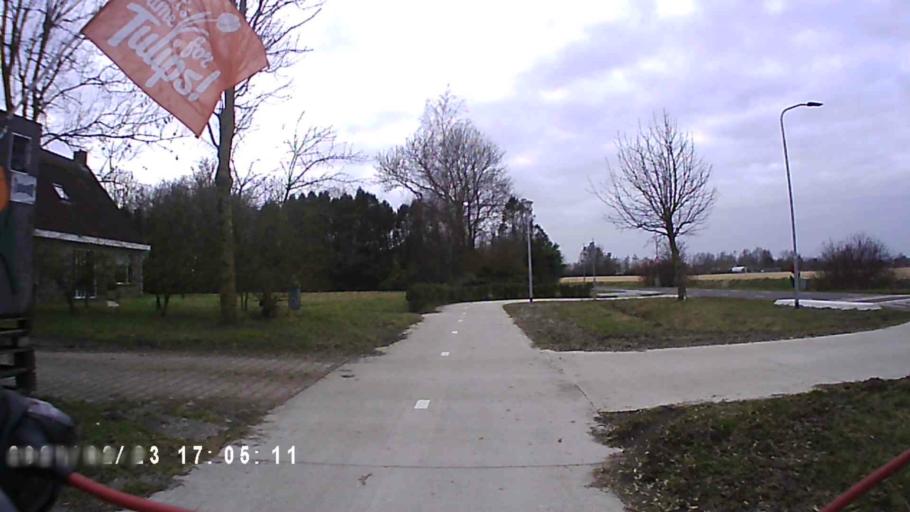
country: NL
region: Groningen
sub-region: Gemeente De Marne
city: Ulrum
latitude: 53.3878
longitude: 6.3793
